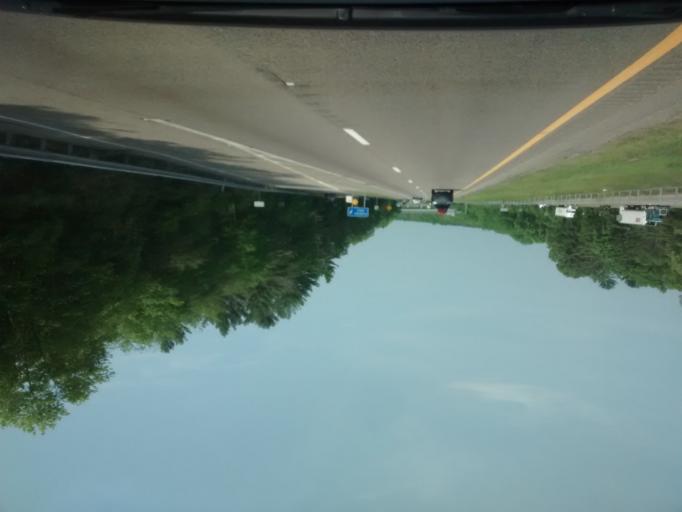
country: US
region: Massachusetts
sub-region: Plymouth County
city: Middleborough Center
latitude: 41.8716
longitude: -70.8951
